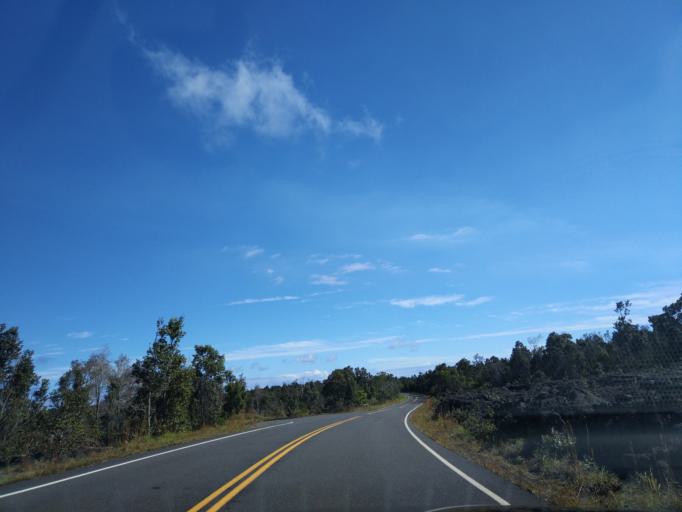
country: US
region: Hawaii
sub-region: Hawaii County
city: Volcano
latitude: 19.3708
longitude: -155.2261
